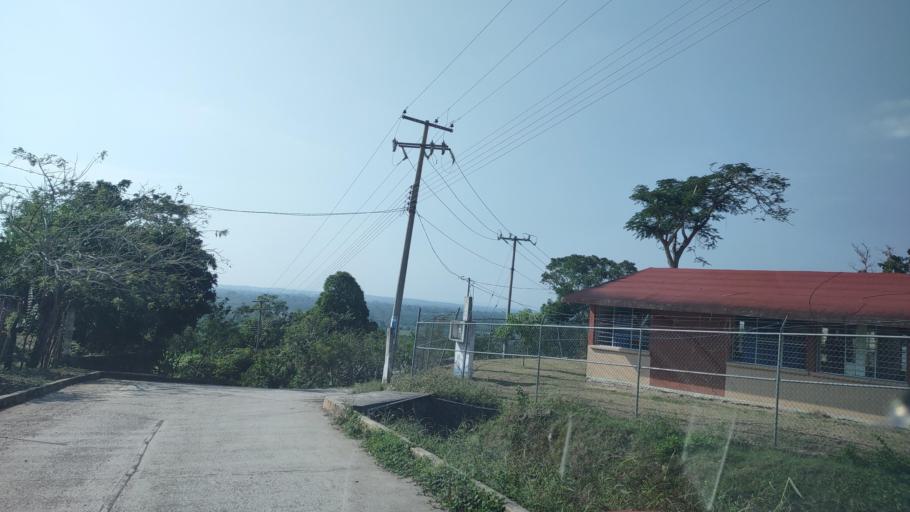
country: MX
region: Veracruz
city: Agua Dulce
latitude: 20.2954
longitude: -97.2820
